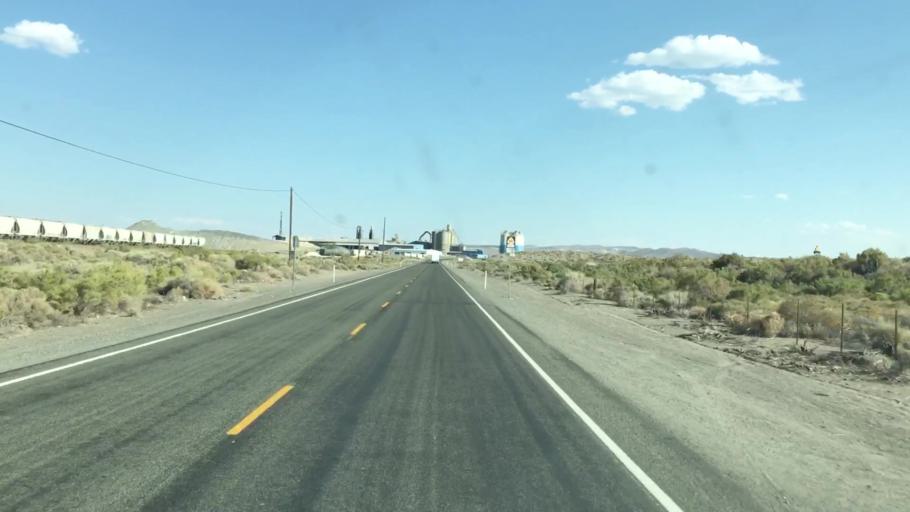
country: US
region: Nevada
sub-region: Lyon County
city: Fernley
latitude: 39.6267
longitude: -119.2725
